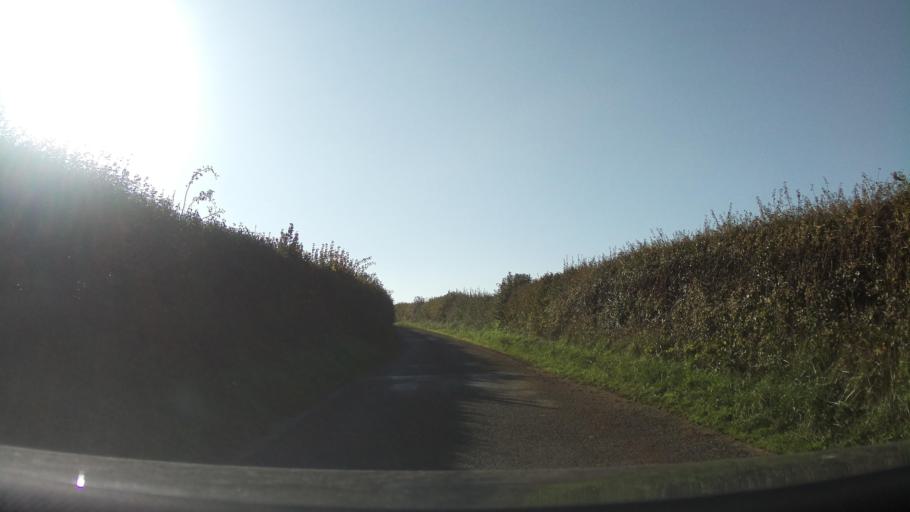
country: GB
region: England
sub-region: Somerset
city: Castle Cary
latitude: 51.0446
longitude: -2.4837
